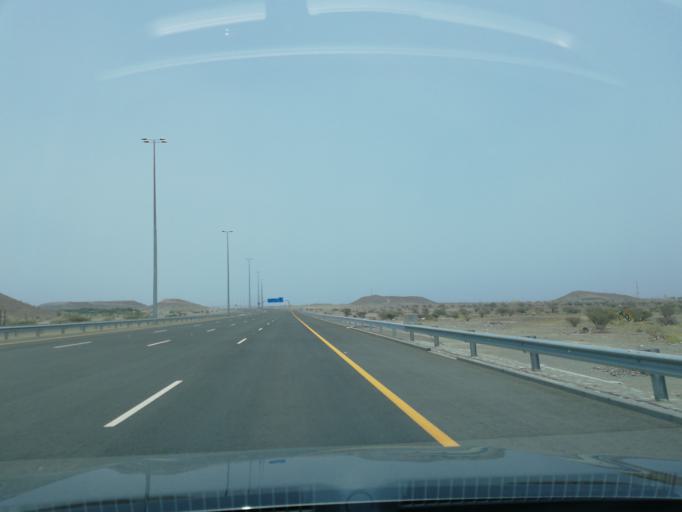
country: OM
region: Al Batinah
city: Al Liwa'
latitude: 24.5106
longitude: 56.5056
